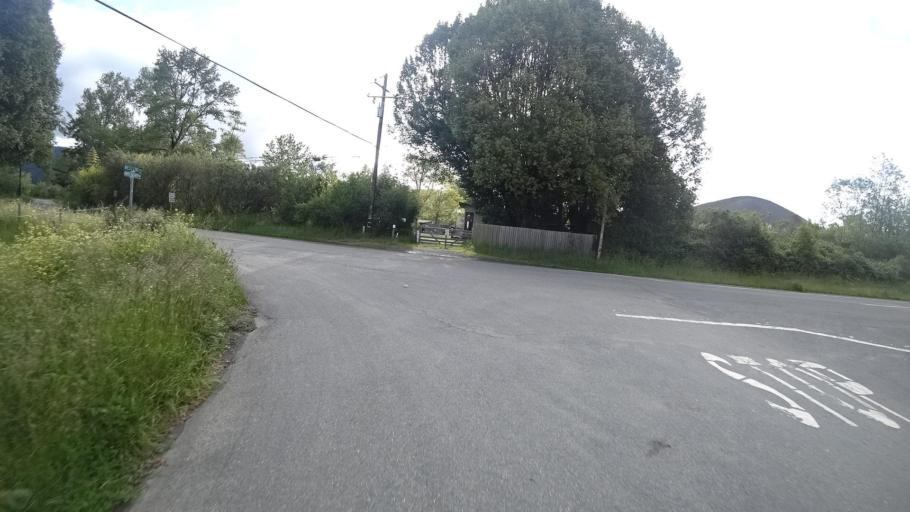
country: US
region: California
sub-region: Humboldt County
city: Blue Lake
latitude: 40.8681
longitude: -123.9957
